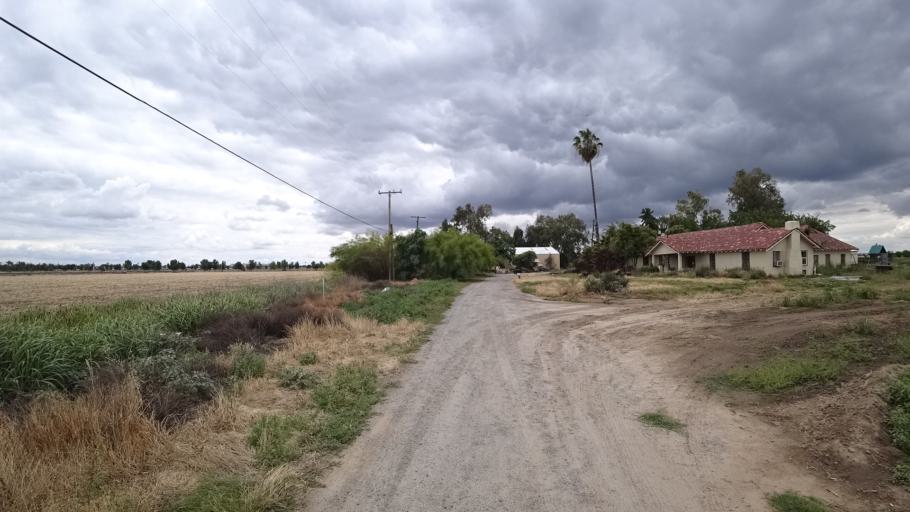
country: US
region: California
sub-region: Kings County
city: Armona
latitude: 36.3231
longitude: -119.6820
